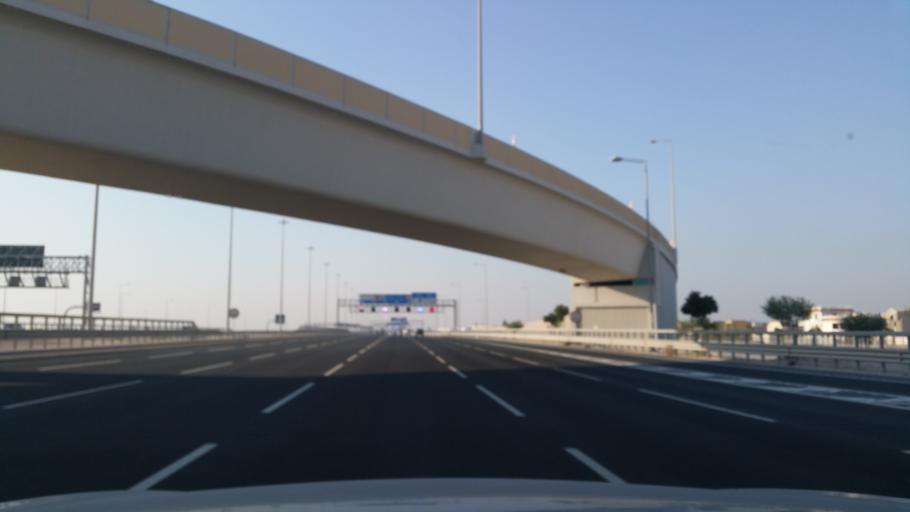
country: QA
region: Al Wakrah
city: Al Wakrah
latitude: 25.1350
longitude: 51.5848
